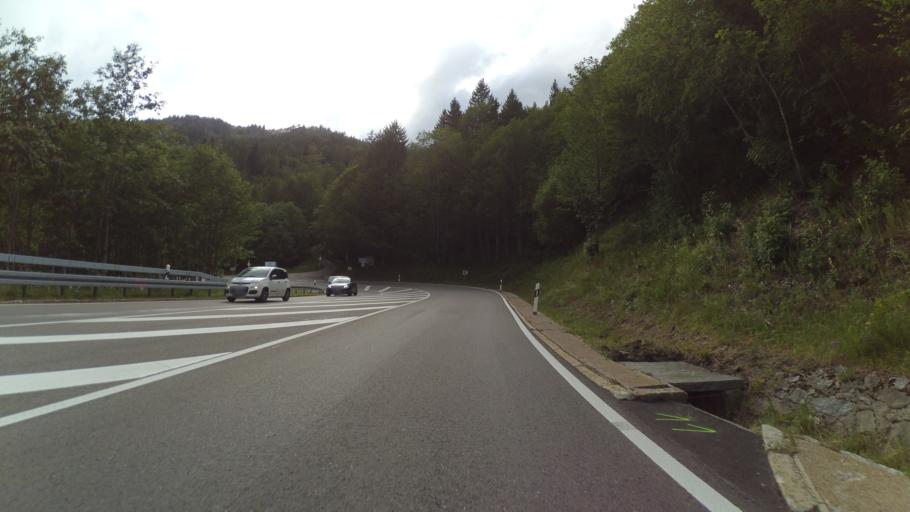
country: DE
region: Baden-Wuerttemberg
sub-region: Freiburg Region
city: Todtnau
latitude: 47.8590
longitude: 7.9980
